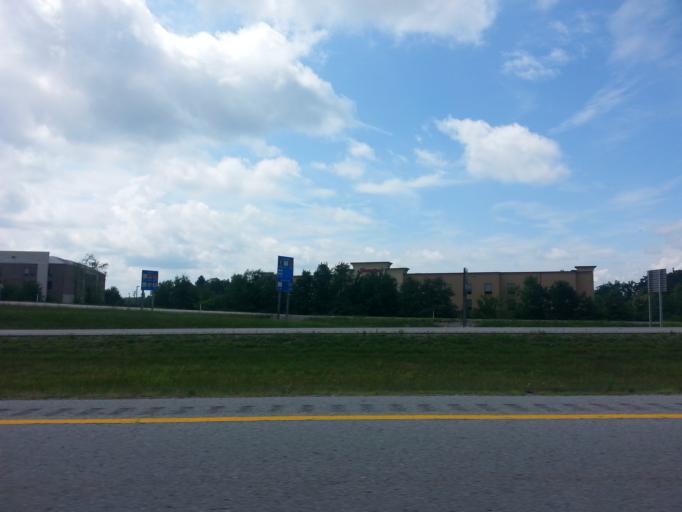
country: US
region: Tennessee
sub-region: Cumberland County
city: Crossville
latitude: 35.9631
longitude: -84.9836
